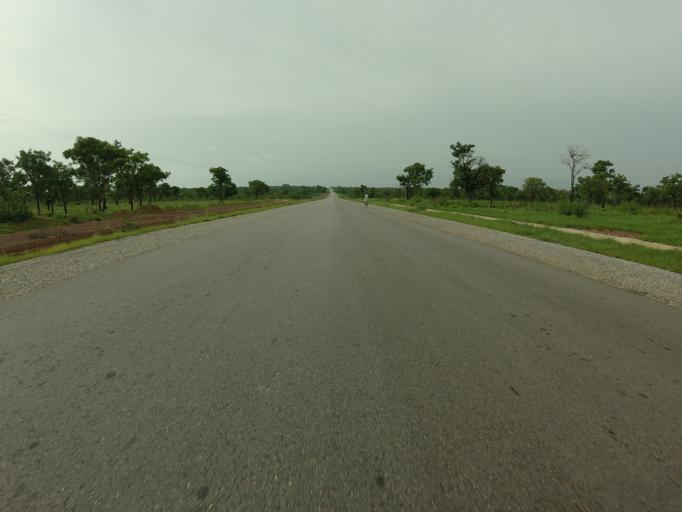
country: GH
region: Northern
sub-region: Yendi
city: Yendi
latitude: 9.6313
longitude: -0.0589
